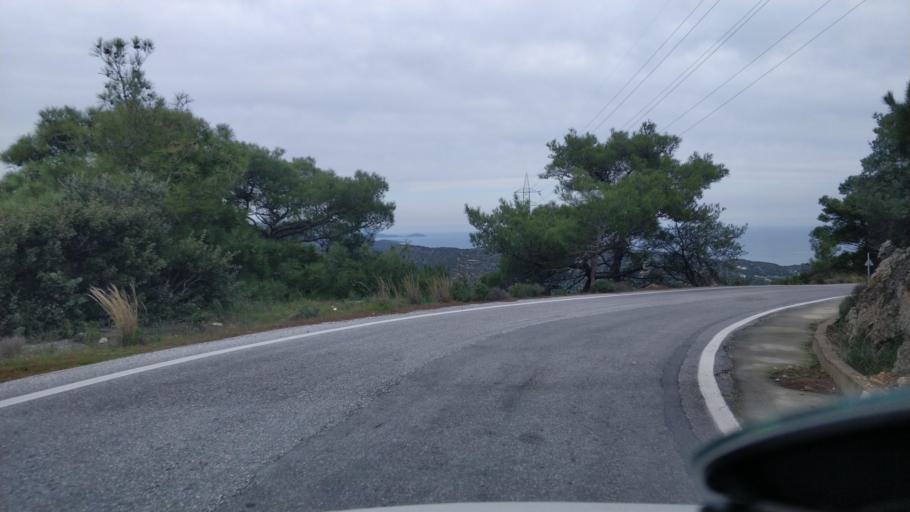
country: GR
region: Crete
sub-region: Nomos Lasithiou
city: Kritsa
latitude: 35.1040
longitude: 25.7020
